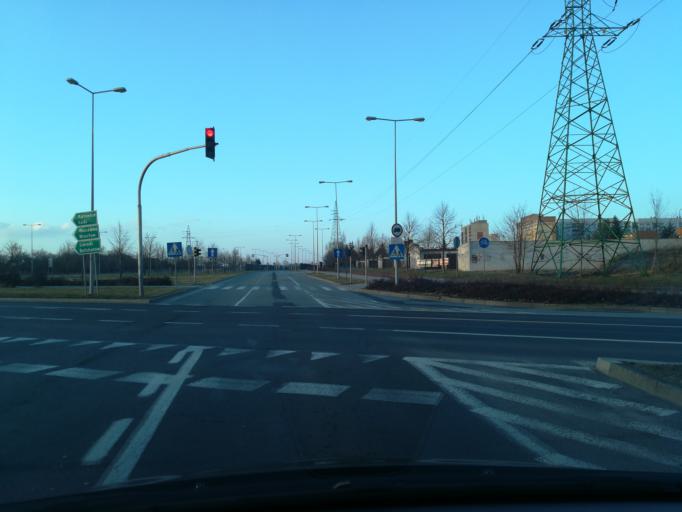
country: PL
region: Lodz Voivodeship
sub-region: Piotrkow Trybunalski
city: Piotrkow Trybunalski
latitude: 51.4063
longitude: 19.6566
